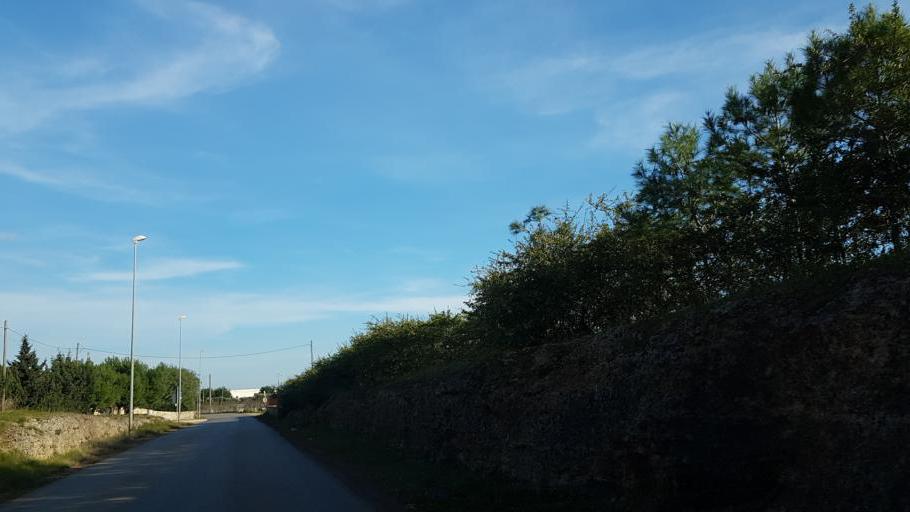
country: IT
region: Apulia
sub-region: Provincia di Brindisi
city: San Vito dei Normanni
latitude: 40.7044
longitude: 17.7151
